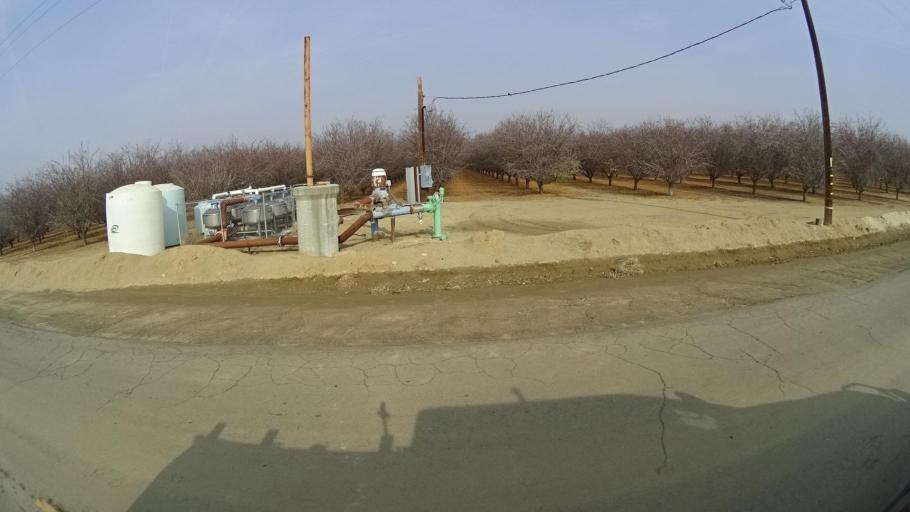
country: US
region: California
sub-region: Kern County
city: Greenfield
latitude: 35.0764
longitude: -119.0407
